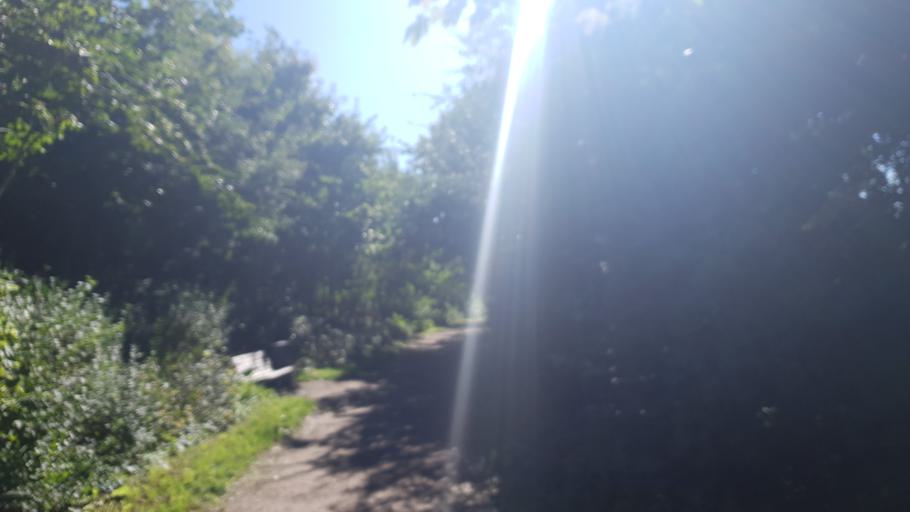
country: DK
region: Zealand
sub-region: Roskilde Kommune
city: Roskilde
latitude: 55.6336
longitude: 12.0826
